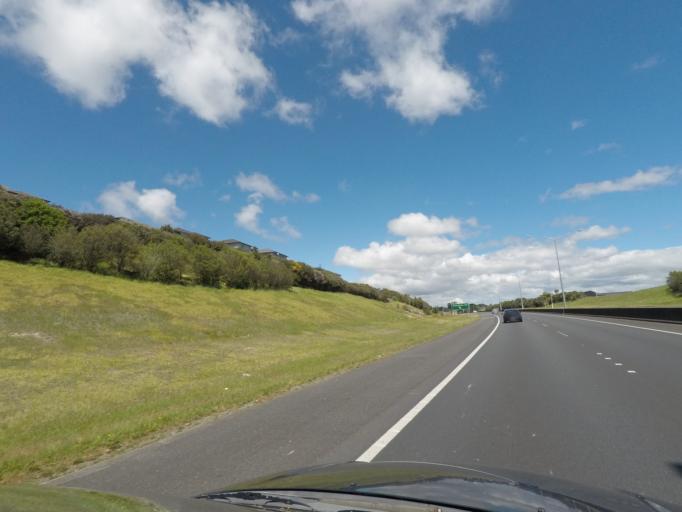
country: NZ
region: Auckland
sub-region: Auckland
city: Rothesay Bay
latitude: -36.7667
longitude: 174.6896
